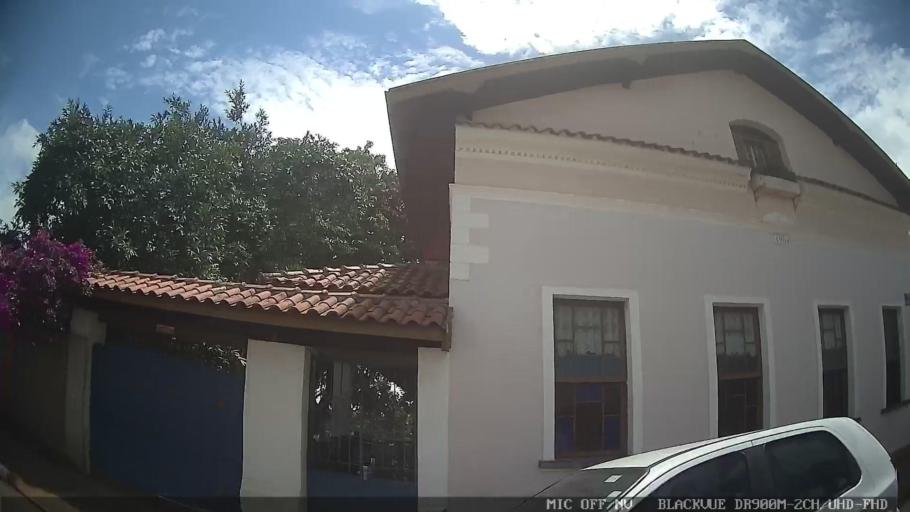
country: BR
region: Sao Paulo
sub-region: Laranjal Paulista
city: Laranjal Paulista
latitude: -23.0527
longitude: -47.8350
